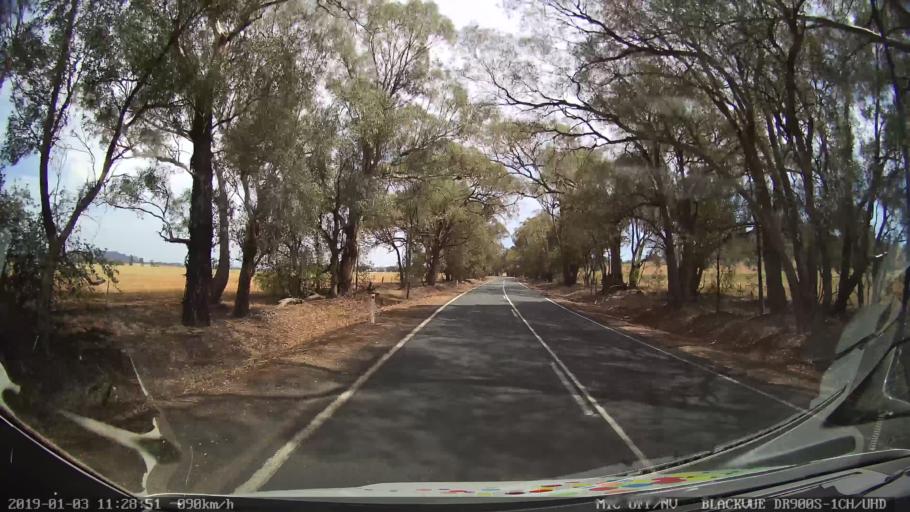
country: AU
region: New South Wales
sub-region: Weddin
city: Grenfell
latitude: -33.9983
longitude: 148.2041
